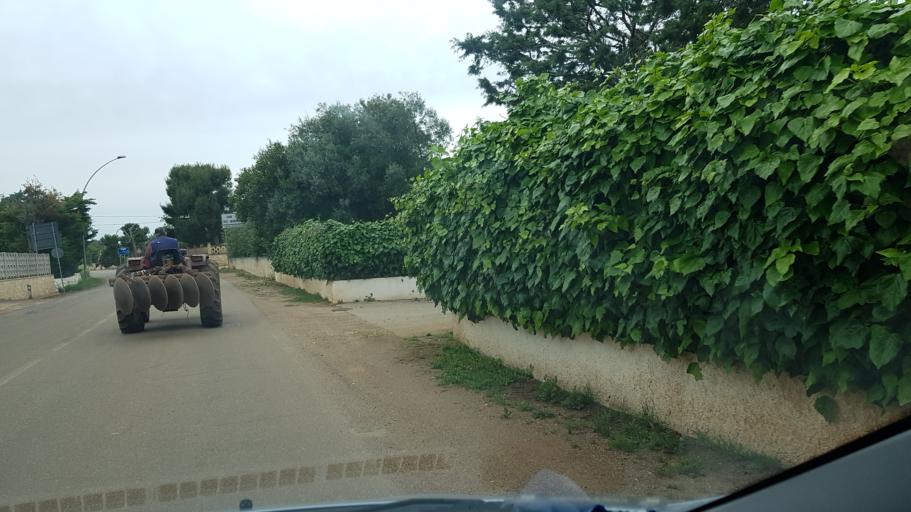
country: IT
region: Apulia
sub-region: Provincia di Brindisi
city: San Vito dei Normanni
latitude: 40.6613
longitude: 17.7187
